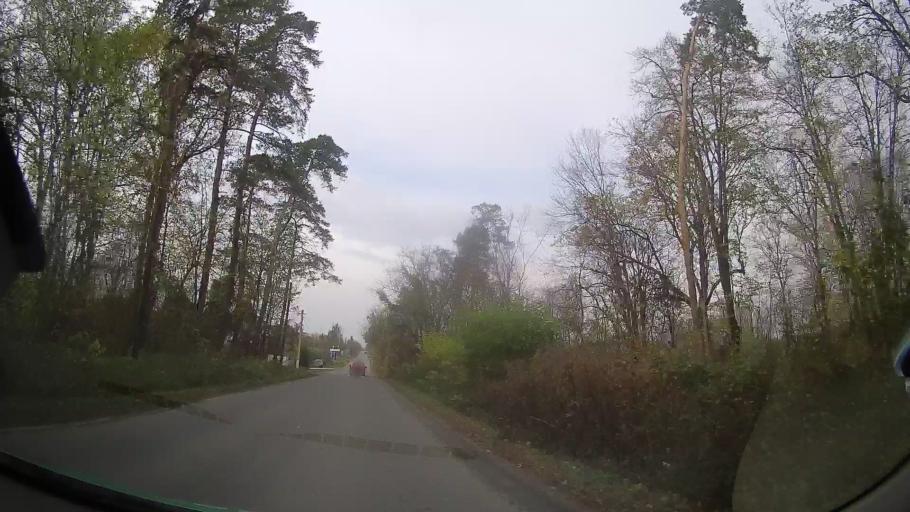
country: RO
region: Prahova
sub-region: Comuna Gorgota
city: Potigrafu
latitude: 44.7706
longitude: 26.1095
